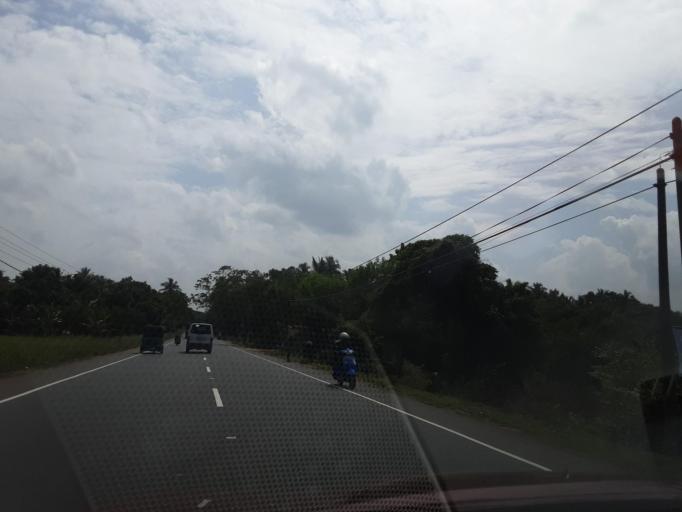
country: LK
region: North Central
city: Anuradhapura
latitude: 8.4984
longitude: 80.5121
